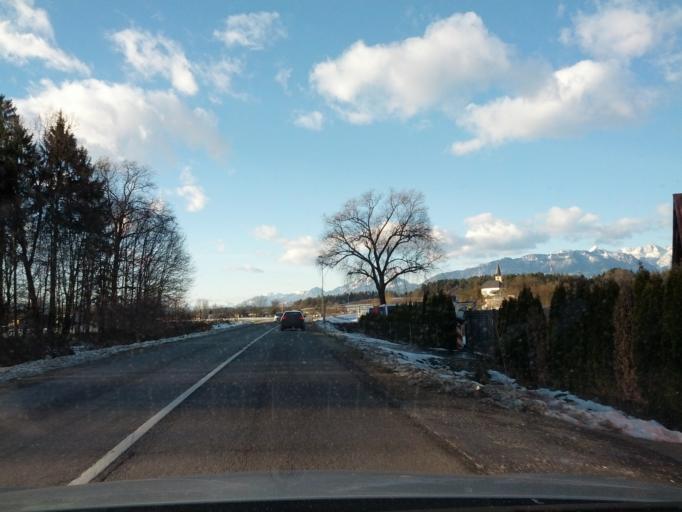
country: SI
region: Domzale
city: Dob
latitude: 46.1454
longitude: 14.6639
